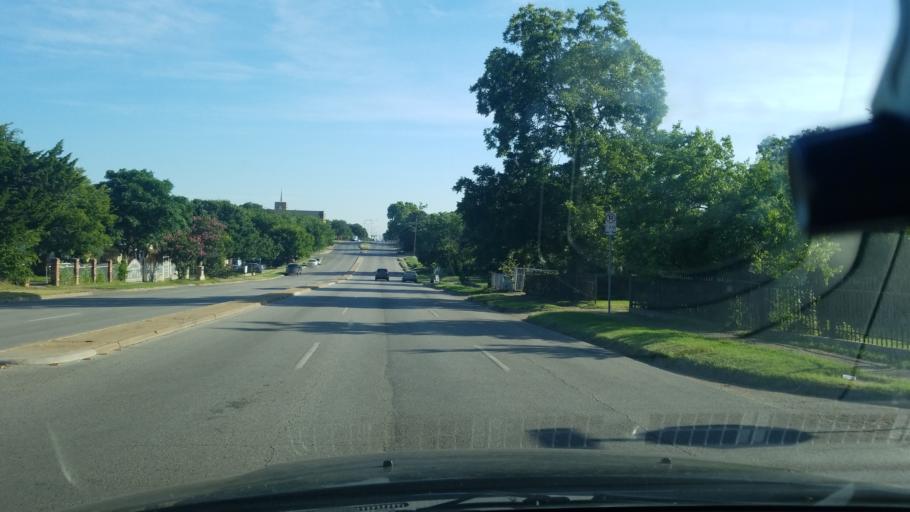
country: US
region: Texas
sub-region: Dallas County
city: Dallas
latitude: 32.7149
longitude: -96.8145
